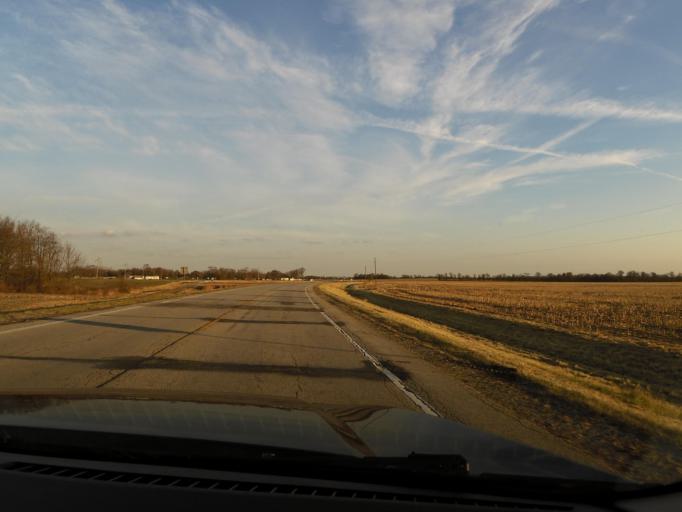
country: US
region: Illinois
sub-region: Fayette County
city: Vandalia
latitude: 38.8604
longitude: -89.0877
